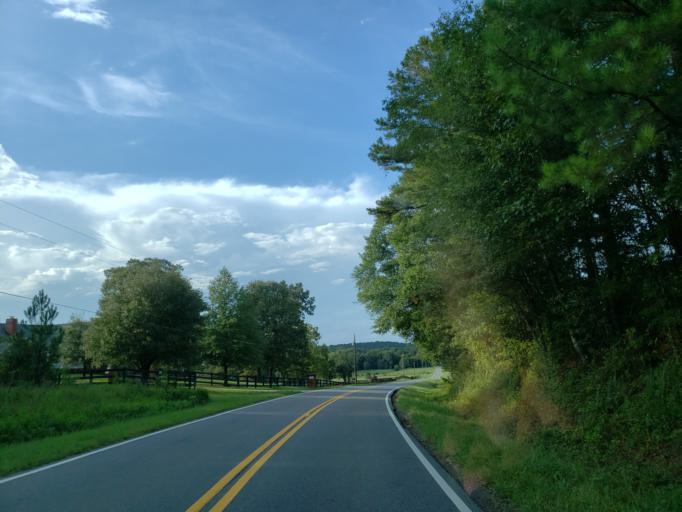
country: US
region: Georgia
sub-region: Bartow County
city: Euharlee
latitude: 34.1956
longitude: -84.9855
